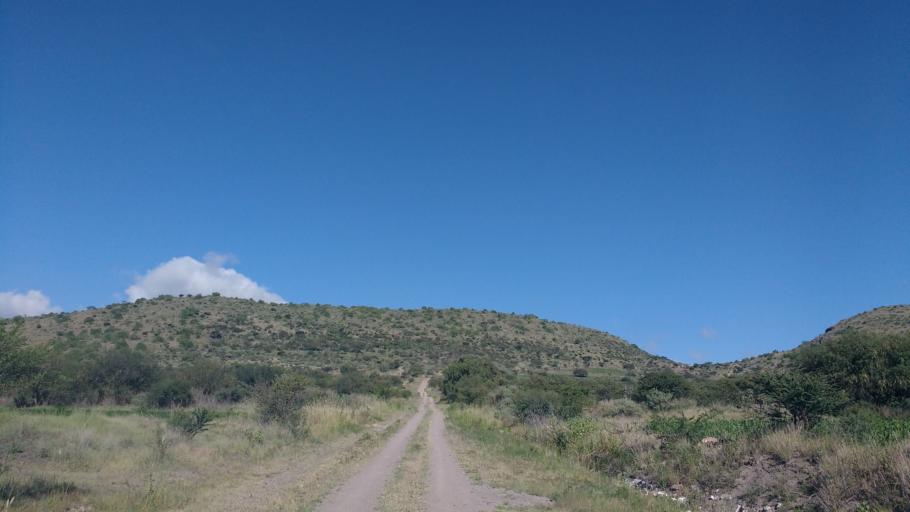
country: MX
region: Hidalgo
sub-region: Tezontepec de Aldama
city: Tenango
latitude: 20.2471
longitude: -99.2744
